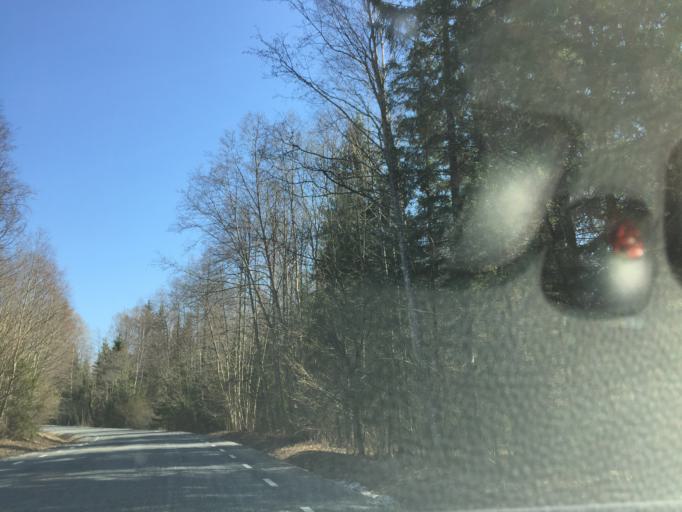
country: EE
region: Tartu
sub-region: Alatskivi vald
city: Kallaste
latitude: 58.5968
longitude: 27.0841
